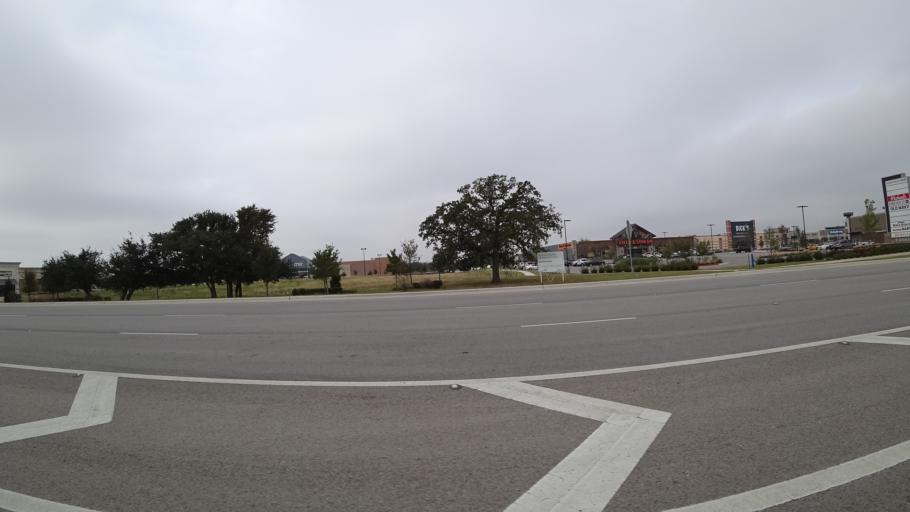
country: US
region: Texas
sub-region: Williamson County
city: Cedar Park
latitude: 30.5305
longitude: -97.8178
